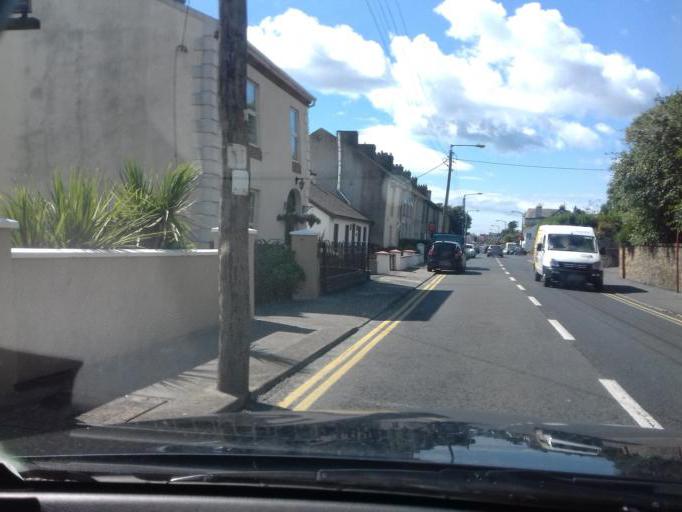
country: IE
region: Munster
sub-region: Waterford
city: Tra Mhor
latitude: 52.1658
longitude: -7.1456
